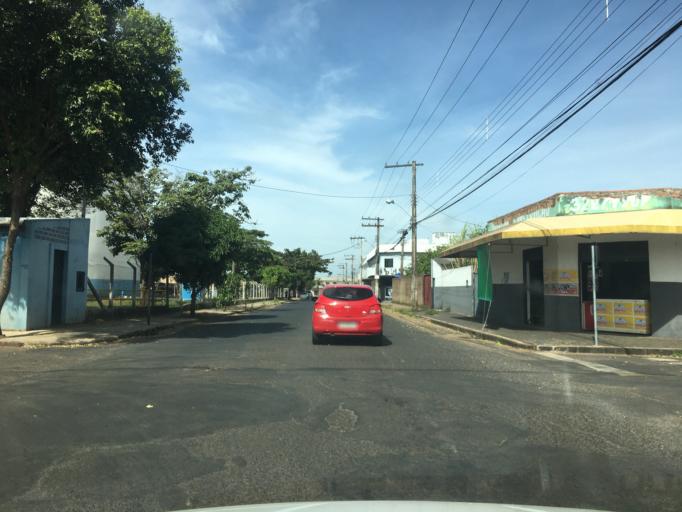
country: BR
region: Minas Gerais
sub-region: Uberlandia
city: Uberlandia
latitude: -18.9435
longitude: -48.3119
